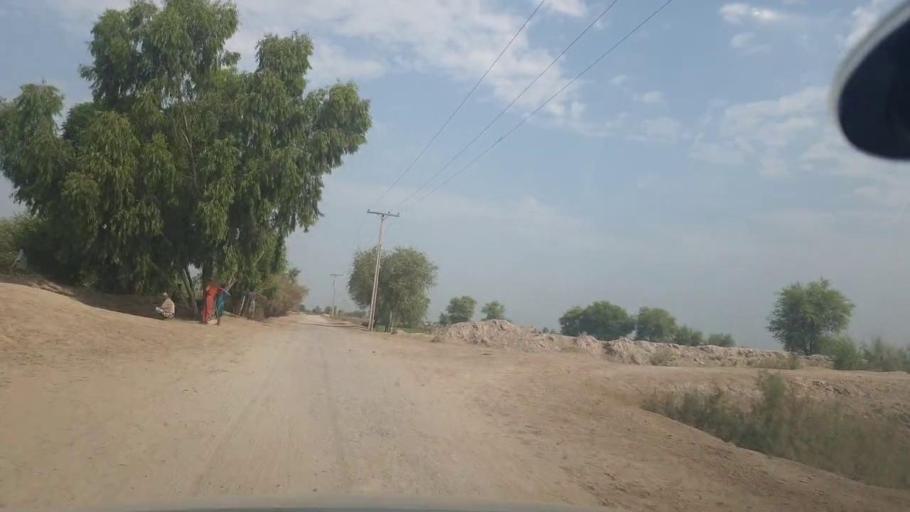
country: PK
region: Balochistan
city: Mehrabpur
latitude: 28.0618
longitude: 68.1046
